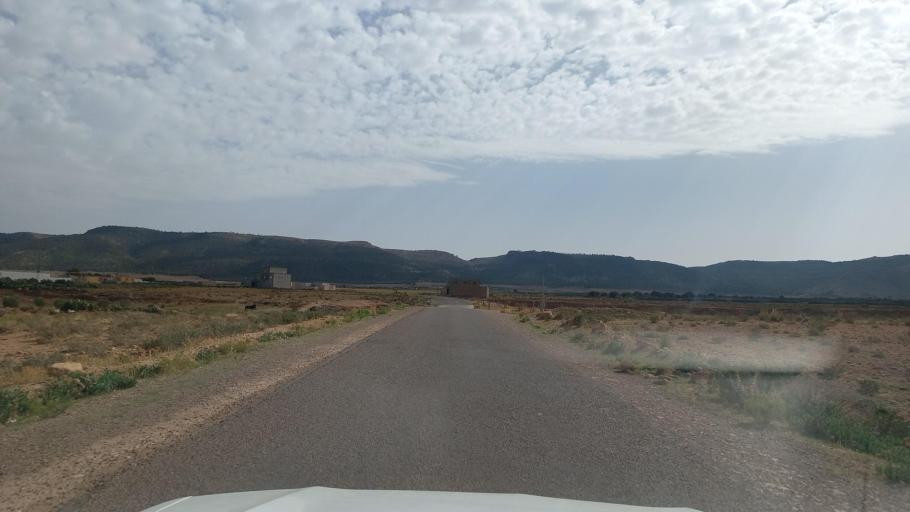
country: TN
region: Al Qasrayn
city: Kasserine
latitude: 35.3569
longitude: 8.8271
